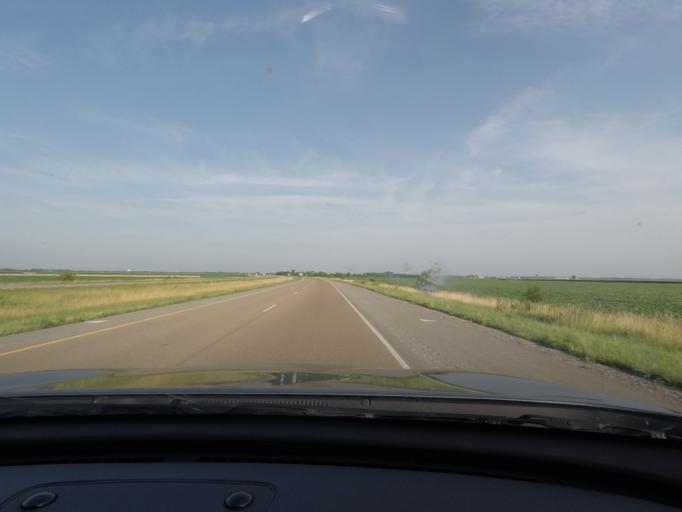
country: US
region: Illinois
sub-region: Washington County
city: Okawville
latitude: 38.4300
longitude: -89.4921
